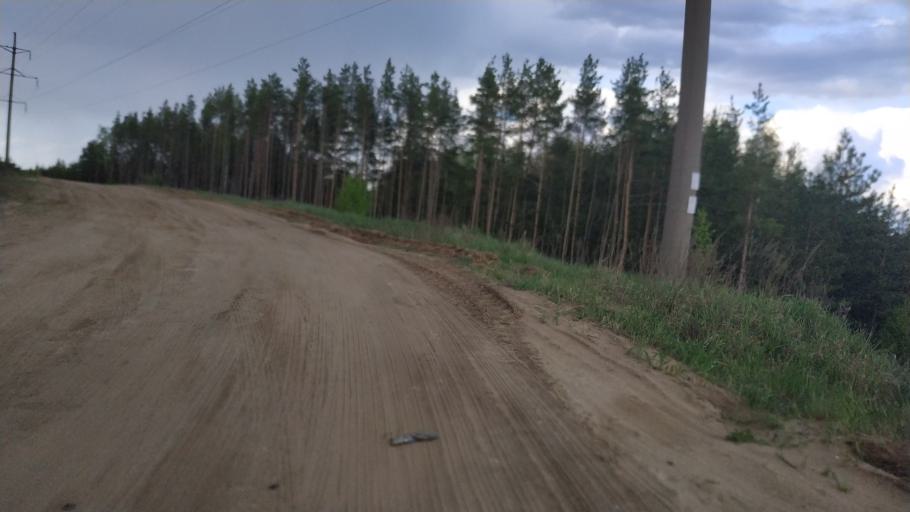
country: RU
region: Chuvashia
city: Novocheboksarsk
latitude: 56.1598
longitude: 47.4668
